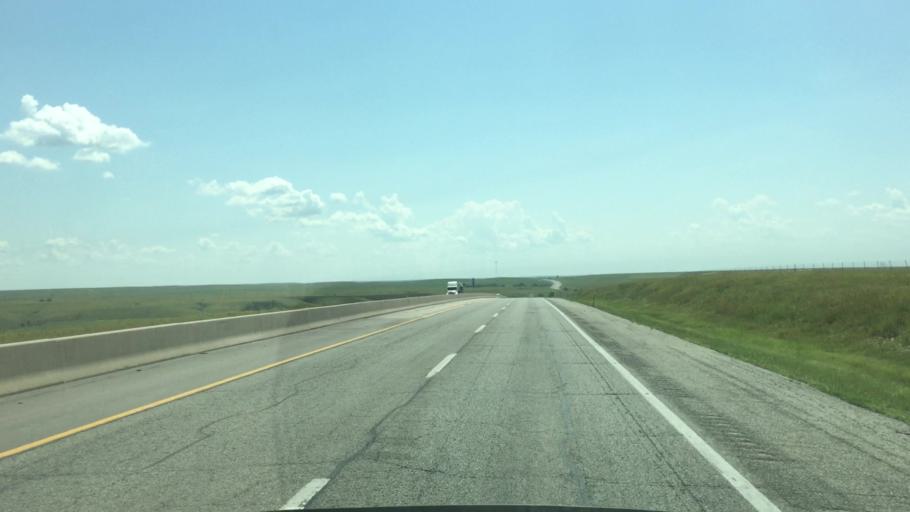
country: US
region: Kansas
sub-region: Chase County
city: Cottonwood Falls
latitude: 38.1869
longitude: -96.4556
